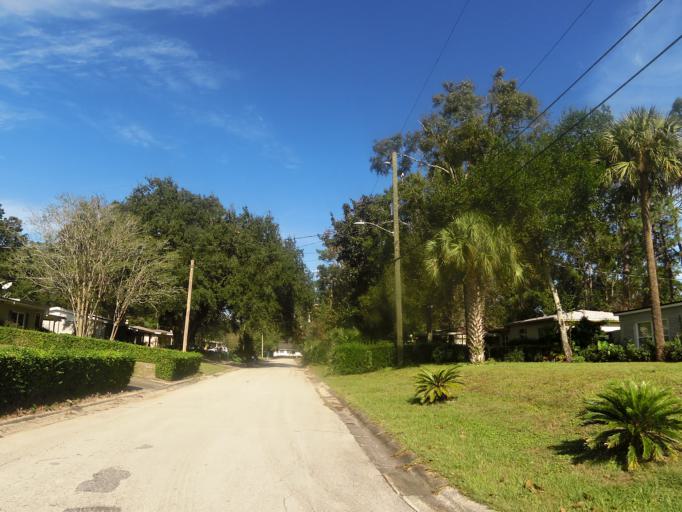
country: US
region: Florida
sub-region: Duval County
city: Jacksonville
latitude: 30.2585
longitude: -81.6323
